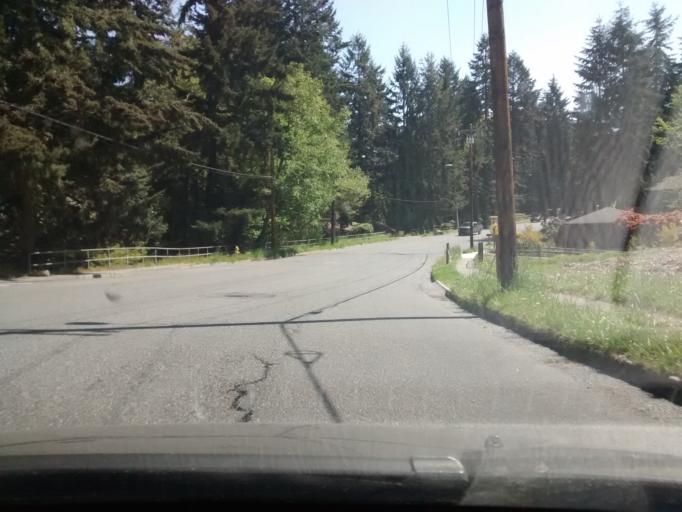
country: US
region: Washington
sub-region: Snohomish County
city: Esperance
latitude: 47.8105
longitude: -122.3506
